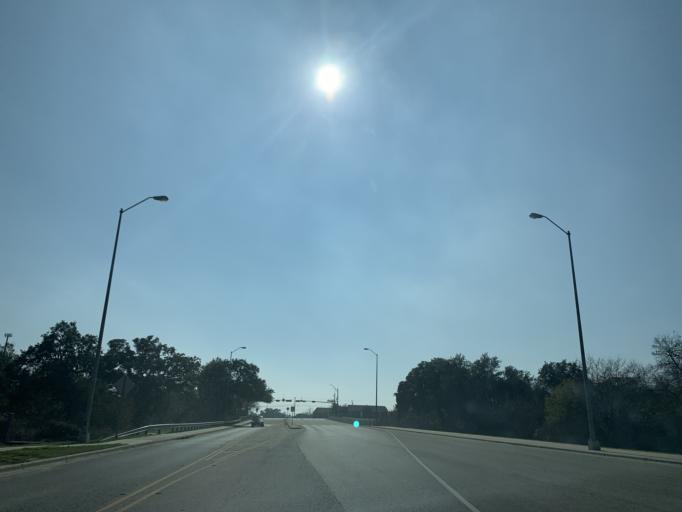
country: US
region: Texas
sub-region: Williamson County
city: Round Rock
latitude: 30.5264
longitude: -97.6412
